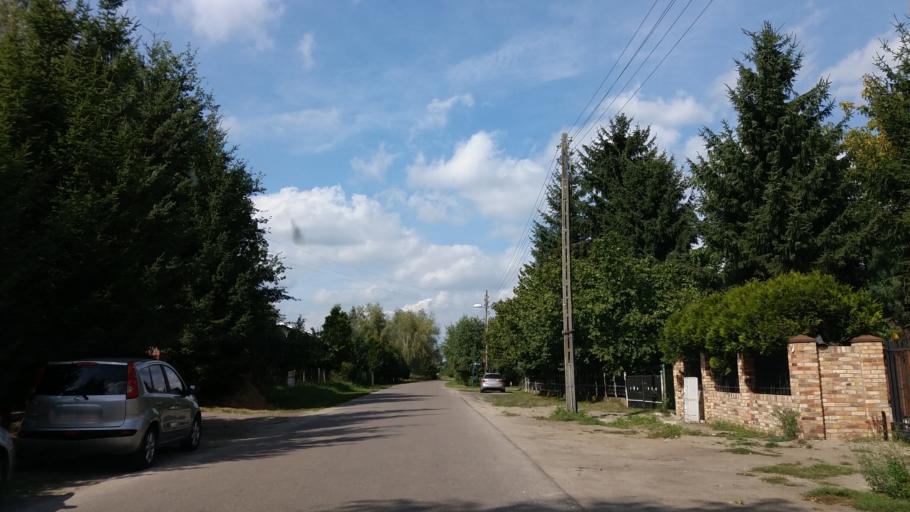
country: PL
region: West Pomeranian Voivodeship
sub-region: Powiat stargardzki
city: Kobylanka
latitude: 53.3511
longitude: 14.9335
